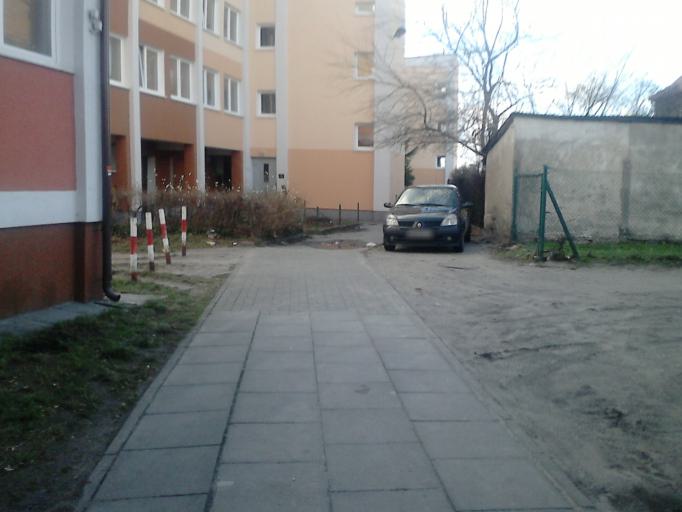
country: PL
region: Pomeranian Voivodeship
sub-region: Gdansk
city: Gdansk
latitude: 54.3639
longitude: 18.7092
